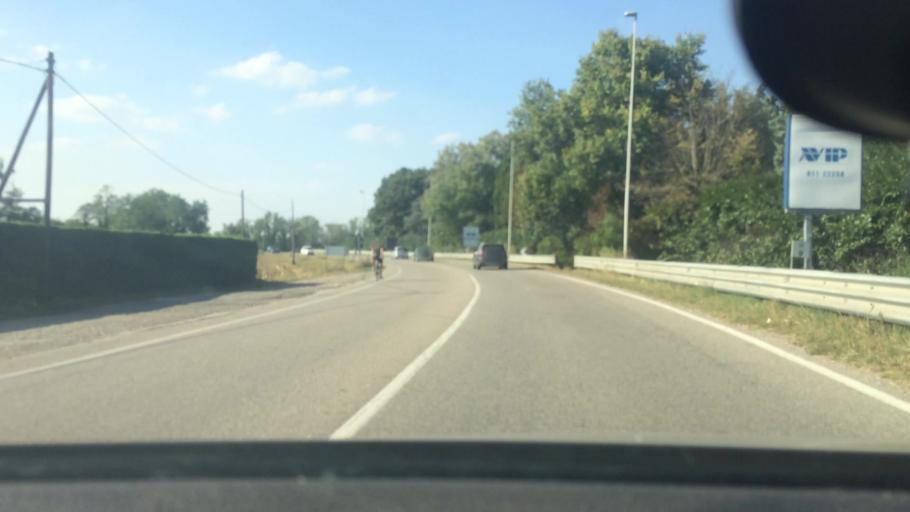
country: IT
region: Lombardy
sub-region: Citta metropolitana di Milano
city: Inveruno
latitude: 45.5219
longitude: 8.8562
